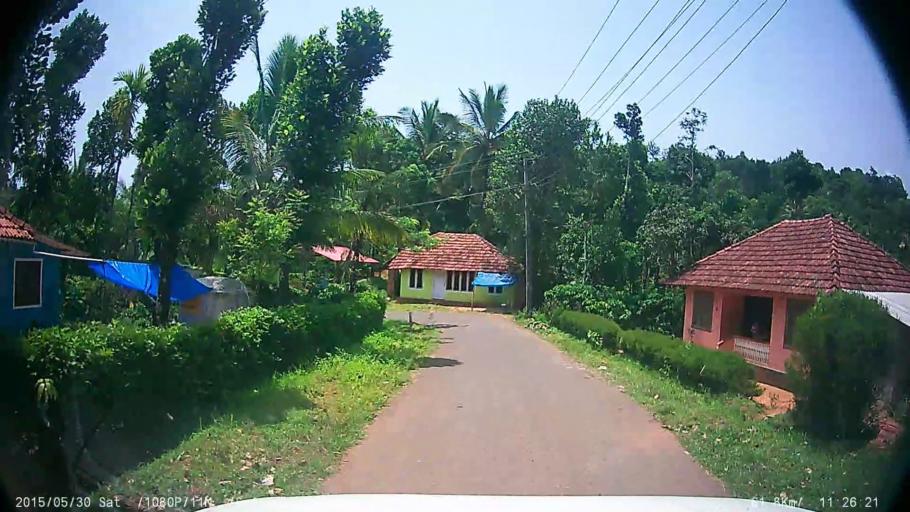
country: IN
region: Kerala
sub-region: Wayanad
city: Panamaram
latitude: 11.8106
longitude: 76.0366
